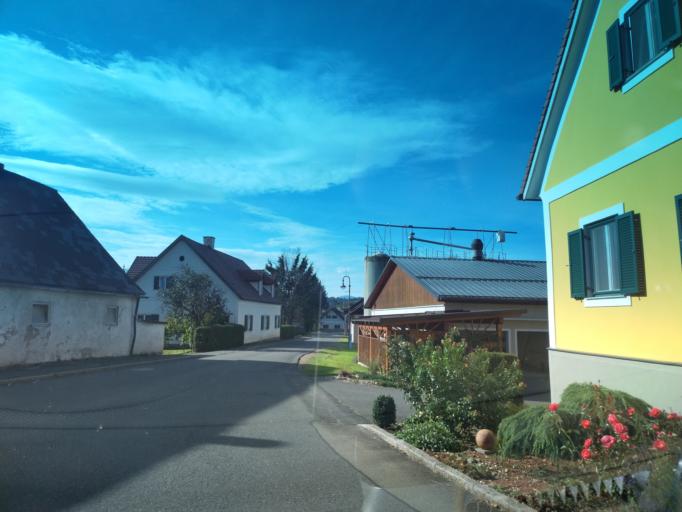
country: AT
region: Styria
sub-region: Politischer Bezirk Leibnitz
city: Sankt Johann im Saggautal
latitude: 46.7044
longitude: 15.4009
